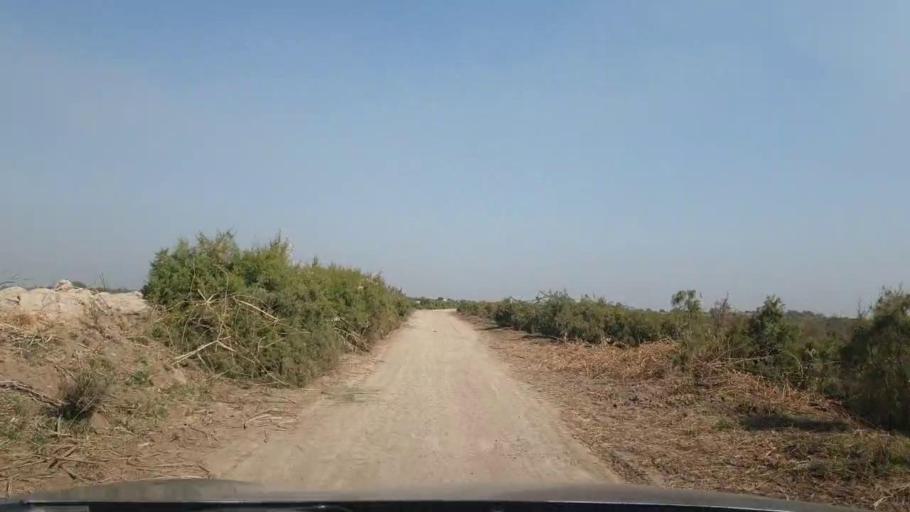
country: PK
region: Sindh
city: Berani
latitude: 25.6561
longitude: 68.8813
